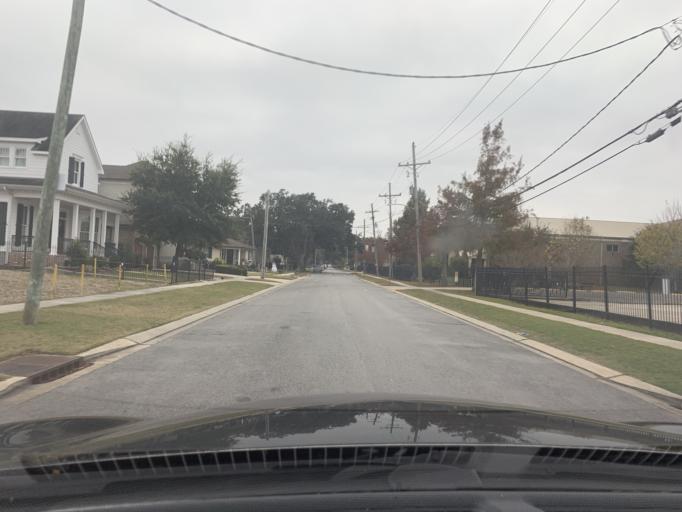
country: US
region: Louisiana
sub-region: Jefferson Parish
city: Metairie
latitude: 30.0195
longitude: -90.1086
